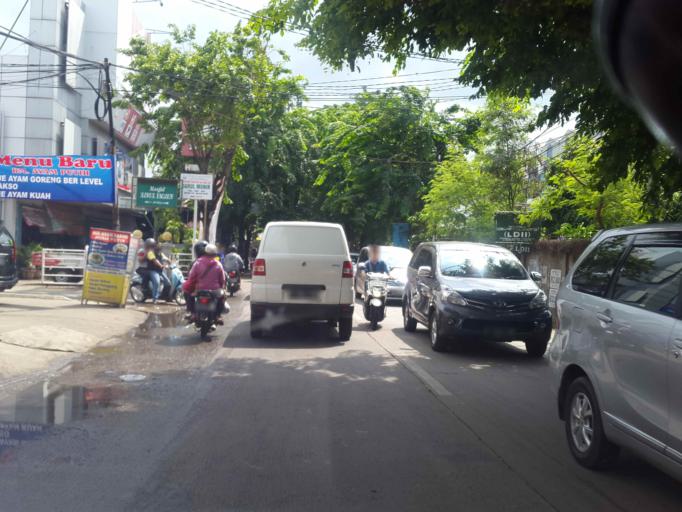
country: ID
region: West Java
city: Bekasi
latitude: -6.2854
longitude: 106.9685
